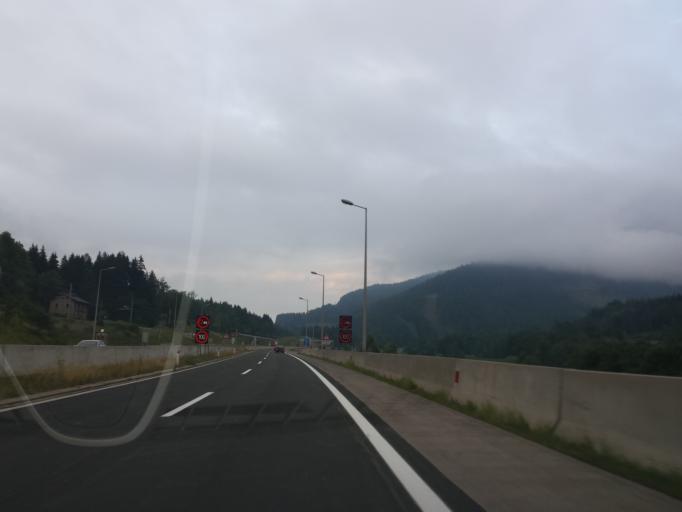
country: AT
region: Lower Austria
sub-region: Politischer Bezirk Neunkirchen
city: Semmering
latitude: 47.6235
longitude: 15.8023
